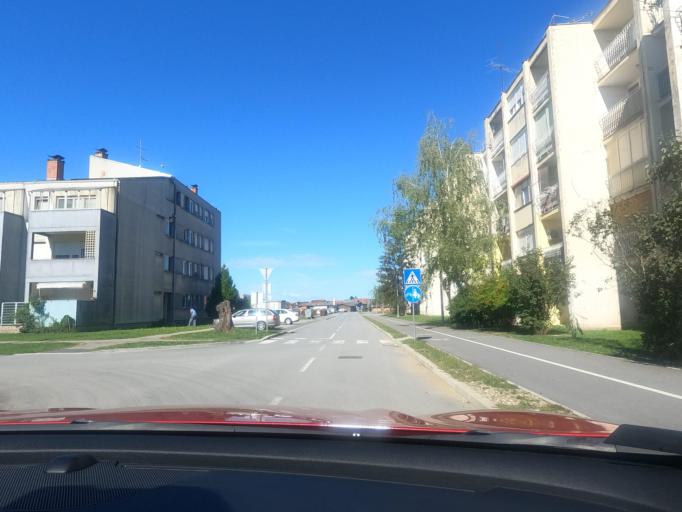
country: HR
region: Sisacko-Moslavacka
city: Petrinja
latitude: 45.4372
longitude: 16.2692
